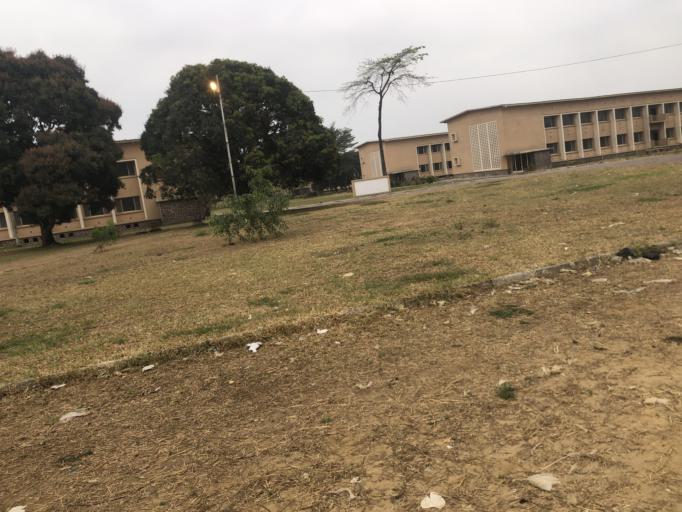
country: CD
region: Kinshasa
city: Masina
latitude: -4.4253
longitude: 15.3097
